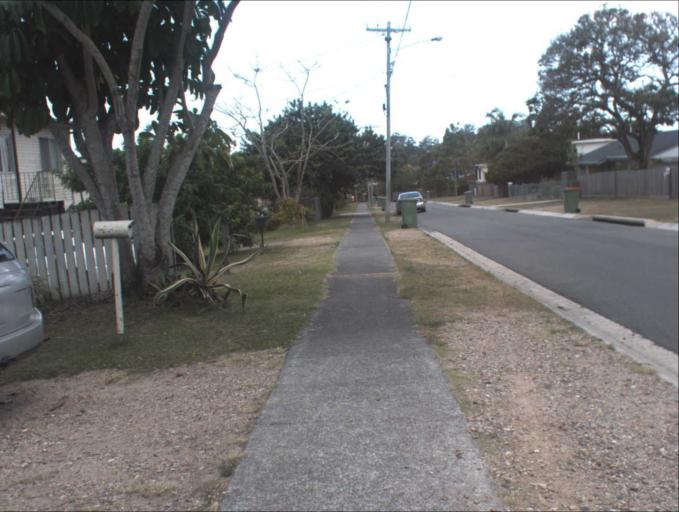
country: AU
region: Queensland
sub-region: Logan
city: Logan City
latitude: -27.6515
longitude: 153.1067
